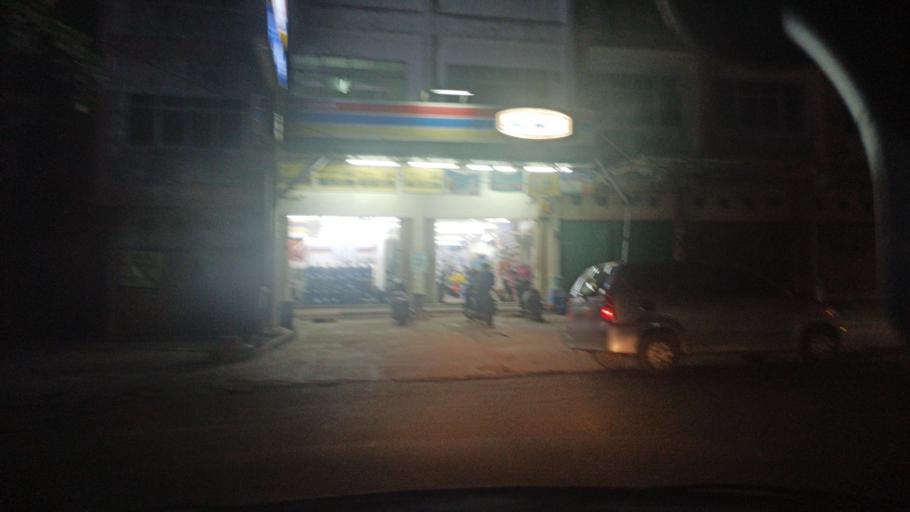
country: ID
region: South Sumatra
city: Palembang
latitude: -2.9311
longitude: 104.7907
